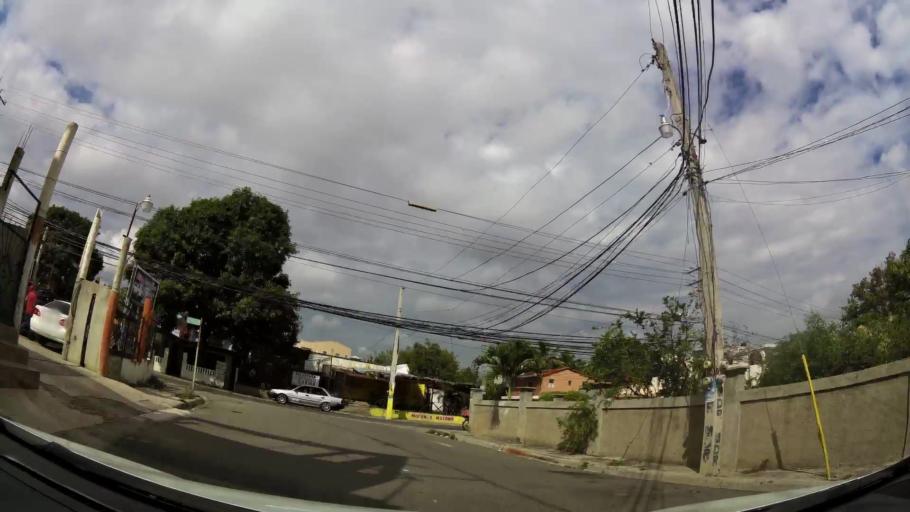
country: DO
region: Santiago
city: Santiago de los Caballeros
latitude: 19.4418
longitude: -70.7069
